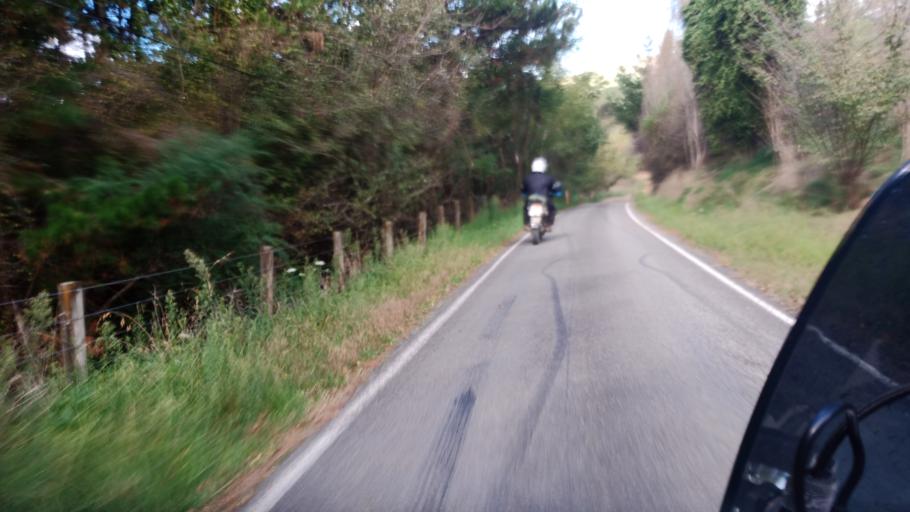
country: NZ
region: Gisborne
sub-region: Gisborne District
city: Gisborne
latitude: -38.4598
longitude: 177.6435
